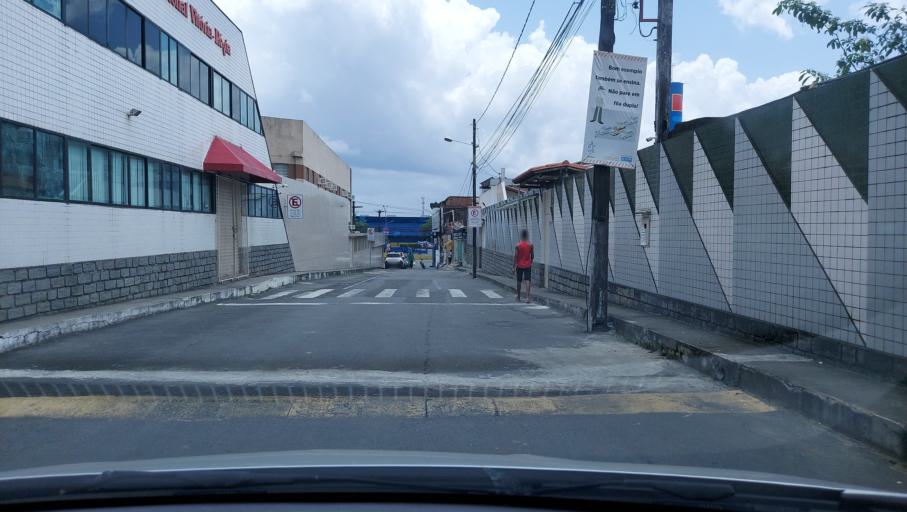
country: BR
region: Bahia
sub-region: Salvador
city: Salvador
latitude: -12.9543
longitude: -38.4610
